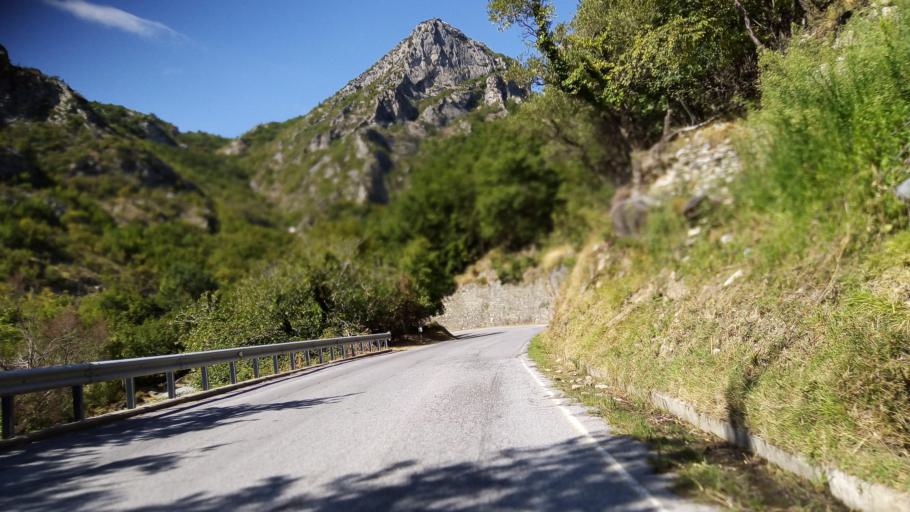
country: IT
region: Liguria
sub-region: Provincia di Savona
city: Toirano
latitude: 44.1387
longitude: 8.1882
